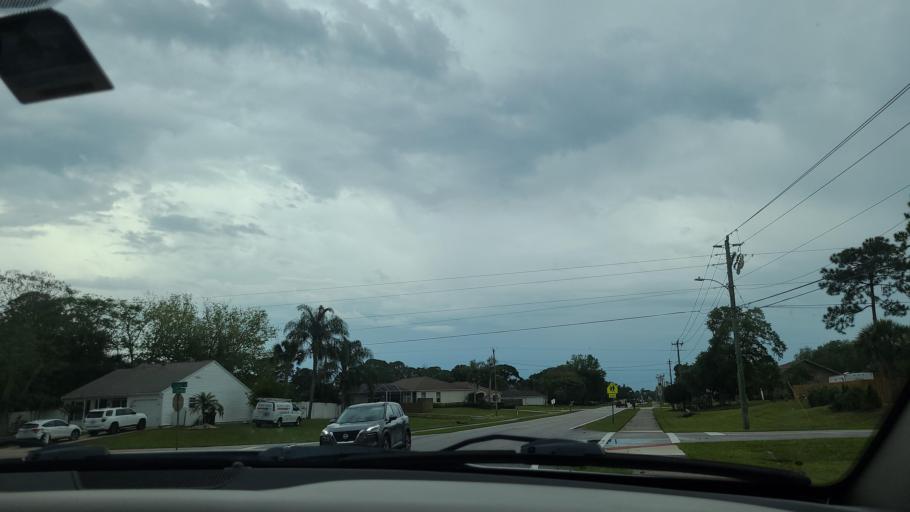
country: US
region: Florida
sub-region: Brevard County
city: West Melbourne
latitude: 28.0291
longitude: -80.6604
